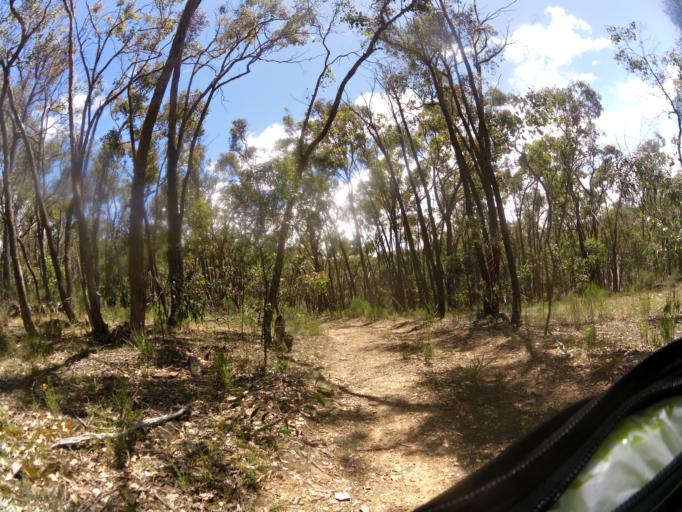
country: AU
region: Victoria
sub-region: Mount Alexander
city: Castlemaine
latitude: -37.0645
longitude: 144.2662
